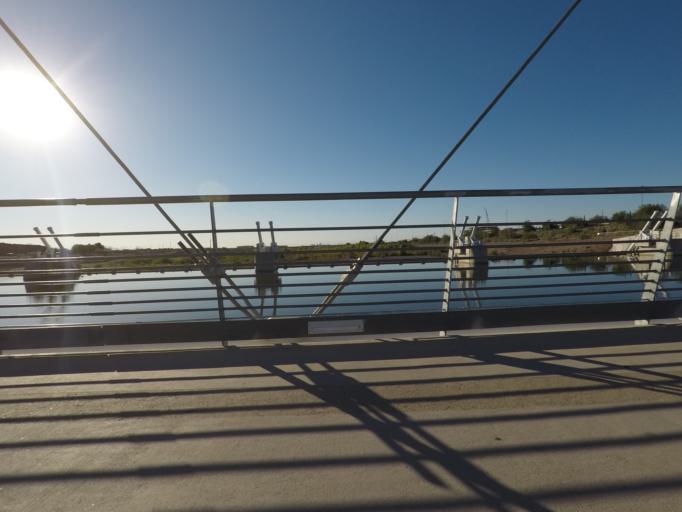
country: US
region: Arizona
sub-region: Maricopa County
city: Tempe Junction
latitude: 33.4334
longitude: -111.9487
